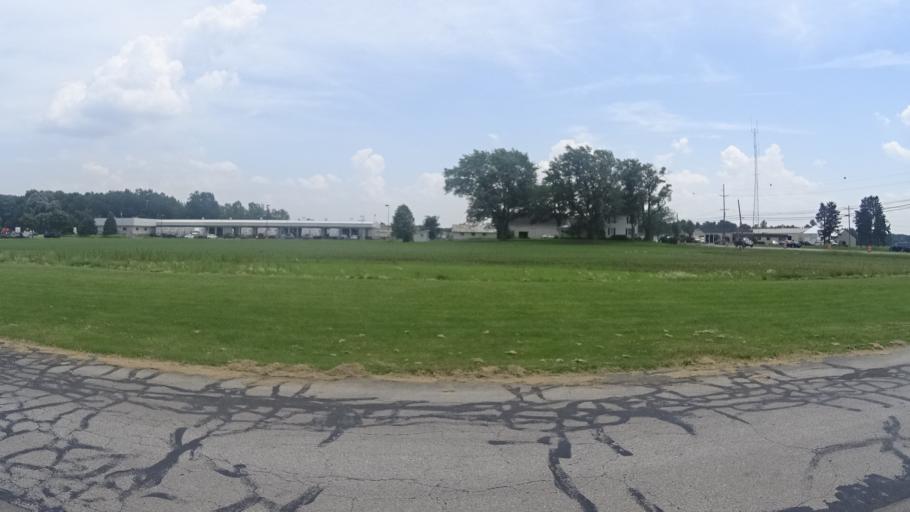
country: US
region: Ohio
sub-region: Erie County
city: Milan
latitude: 41.3175
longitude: -82.6110
